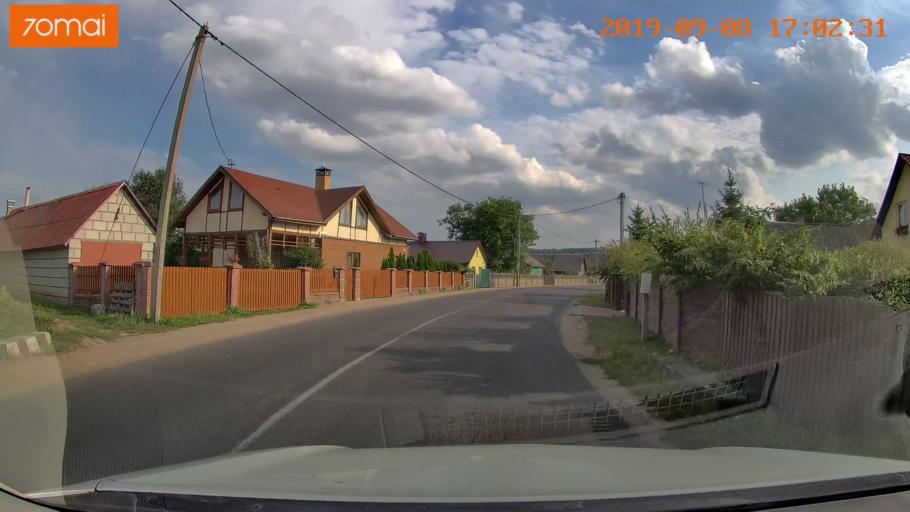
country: BY
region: Grodnenskaya
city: Hrodna
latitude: 53.7030
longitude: 23.9399
